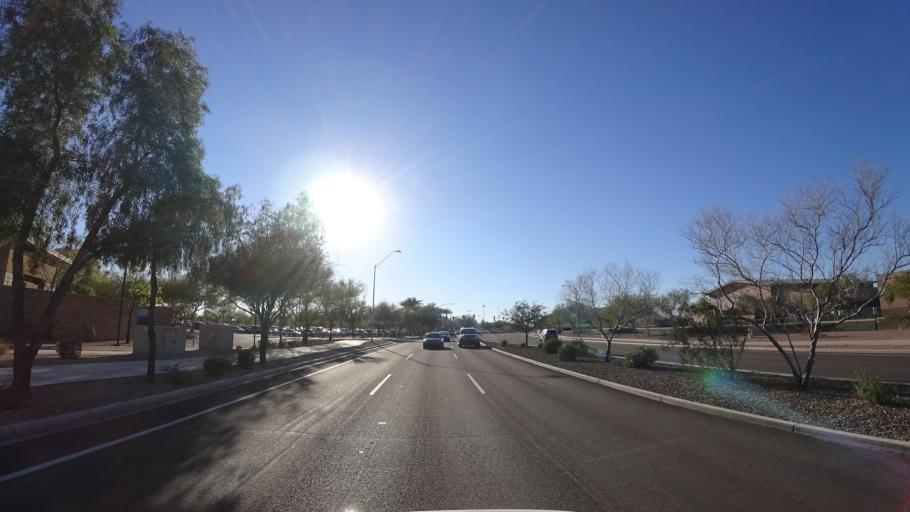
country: US
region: Arizona
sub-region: Maricopa County
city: Sun City
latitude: 33.7111
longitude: -112.2090
